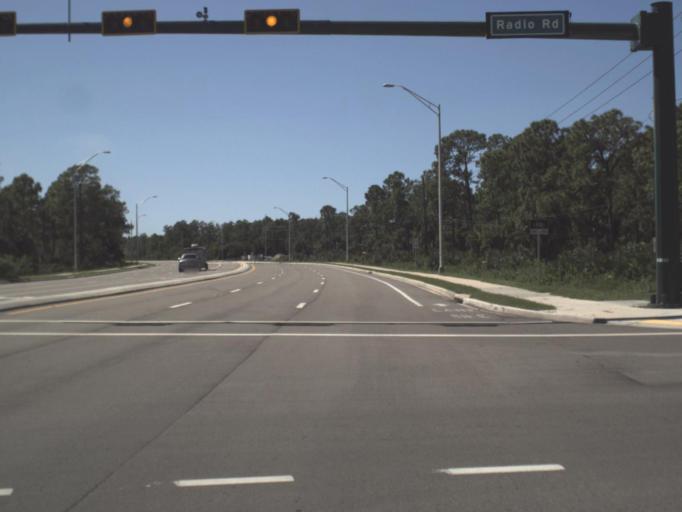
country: US
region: Florida
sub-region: Collier County
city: Golden Gate
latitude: 26.1533
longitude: -81.6979
